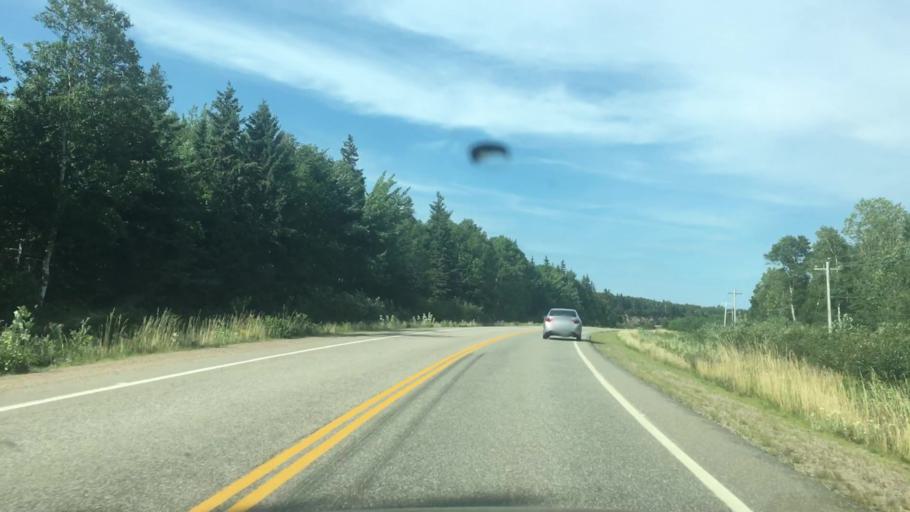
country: CA
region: Nova Scotia
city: Sydney Mines
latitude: 46.7162
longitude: -60.3525
